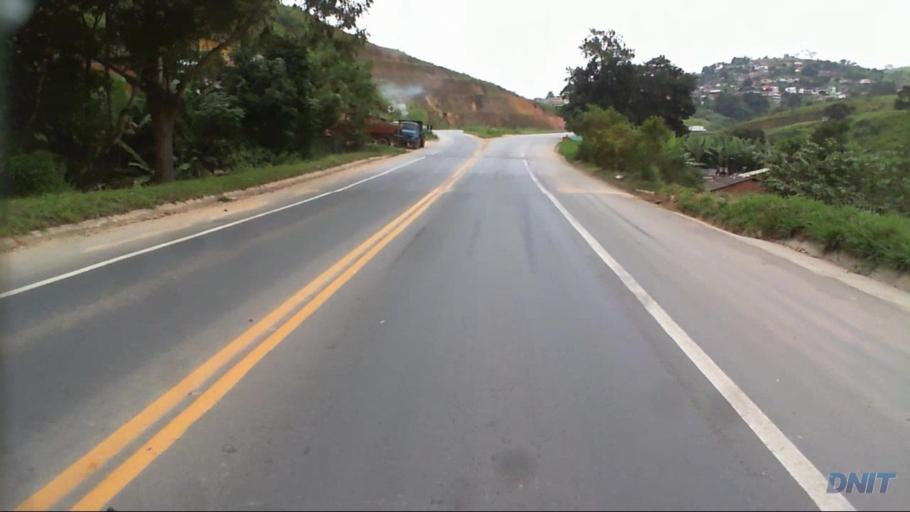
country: BR
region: Minas Gerais
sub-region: Nova Era
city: Nova Era
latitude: -19.7499
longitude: -43.0248
